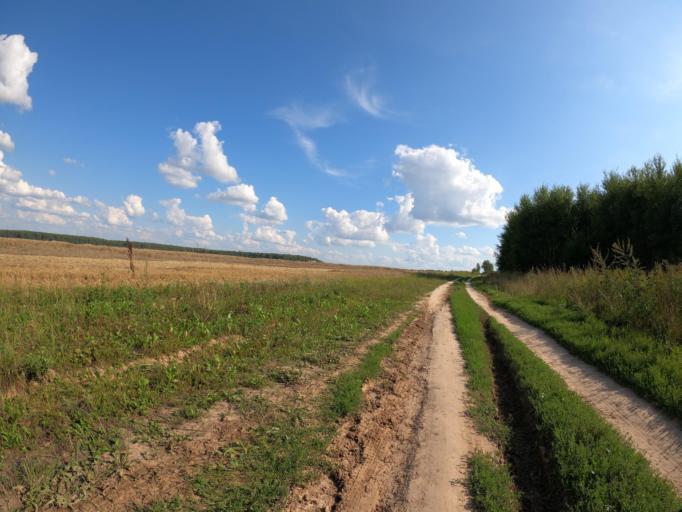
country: RU
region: Moskovskaya
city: Troitskoye
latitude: 55.2259
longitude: 38.4858
